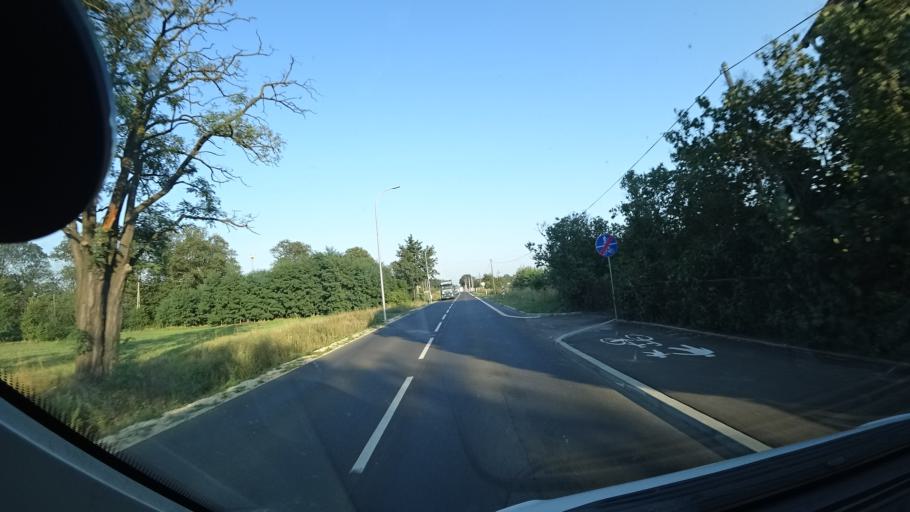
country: PL
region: Opole Voivodeship
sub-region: Powiat kedzierzynsko-kozielski
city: Bierawa
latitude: 50.2919
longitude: 18.2561
